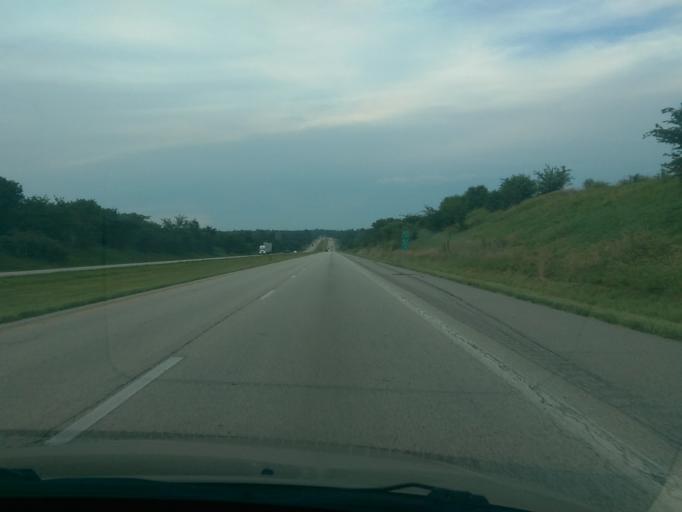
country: US
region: Missouri
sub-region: Andrew County
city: Country Club Village
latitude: 39.8312
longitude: -94.8051
